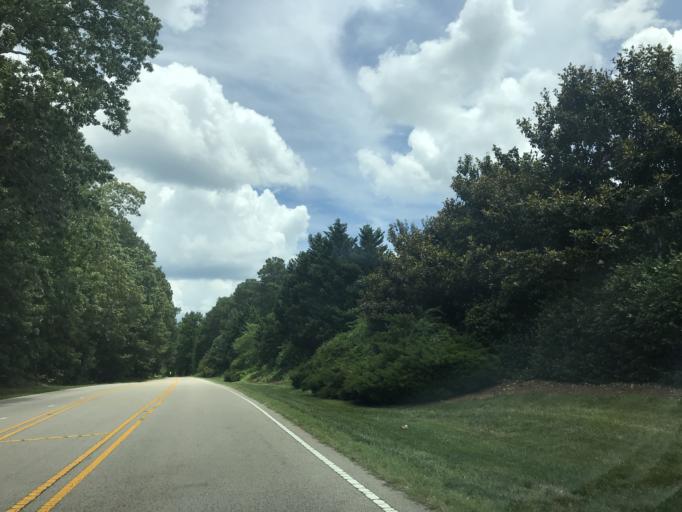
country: US
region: North Carolina
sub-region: Wake County
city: West Raleigh
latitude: 35.9105
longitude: -78.6720
